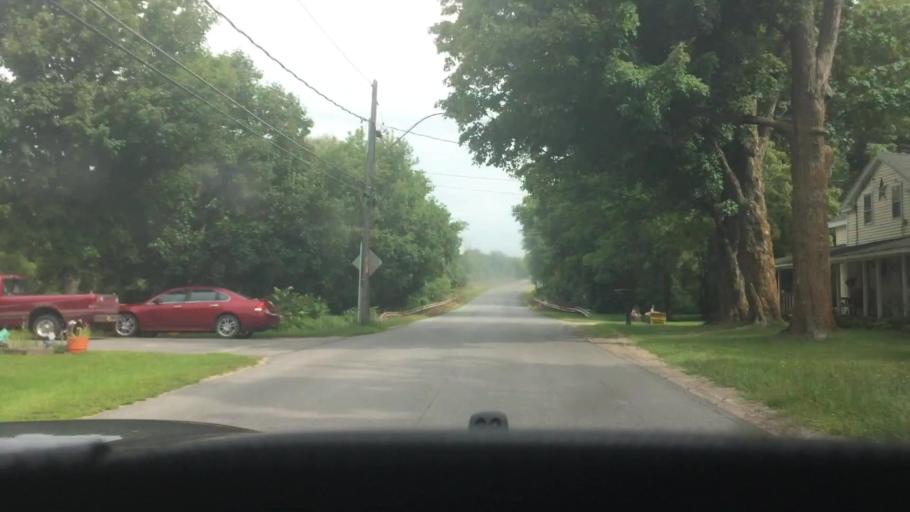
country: US
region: New York
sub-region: St. Lawrence County
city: Canton
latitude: 44.4709
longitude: -75.2296
